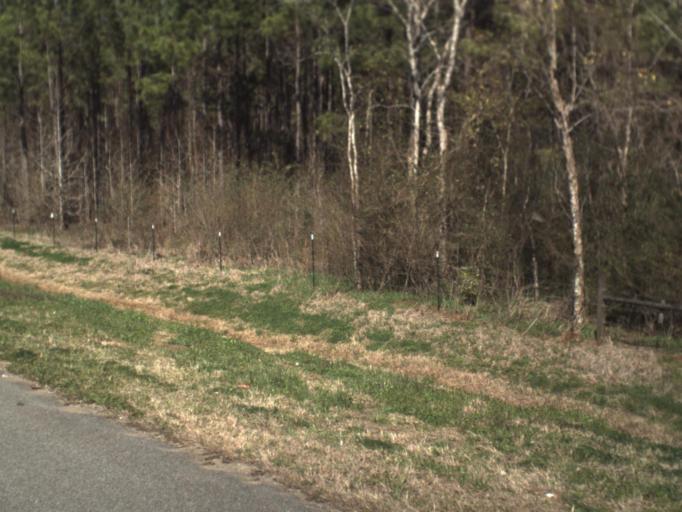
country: US
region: Florida
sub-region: Jackson County
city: Marianna
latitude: 30.8247
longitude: -85.3287
